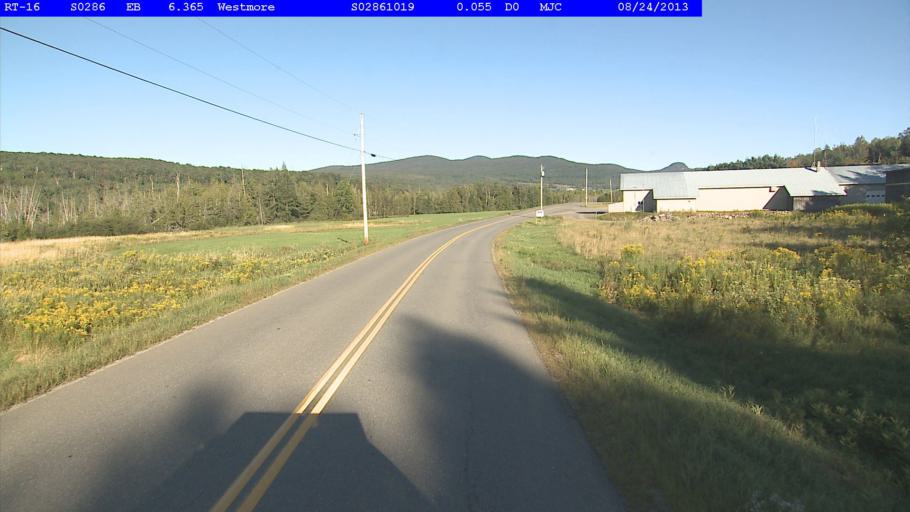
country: US
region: Vermont
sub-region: Orleans County
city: Newport
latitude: 44.7812
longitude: -72.0816
